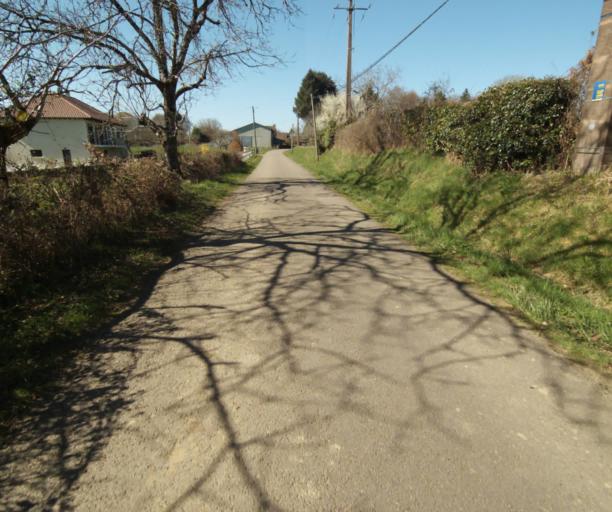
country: FR
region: Limousin
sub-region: Departement de la Correze
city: Tulle
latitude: 45.2780
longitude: 1.7223
